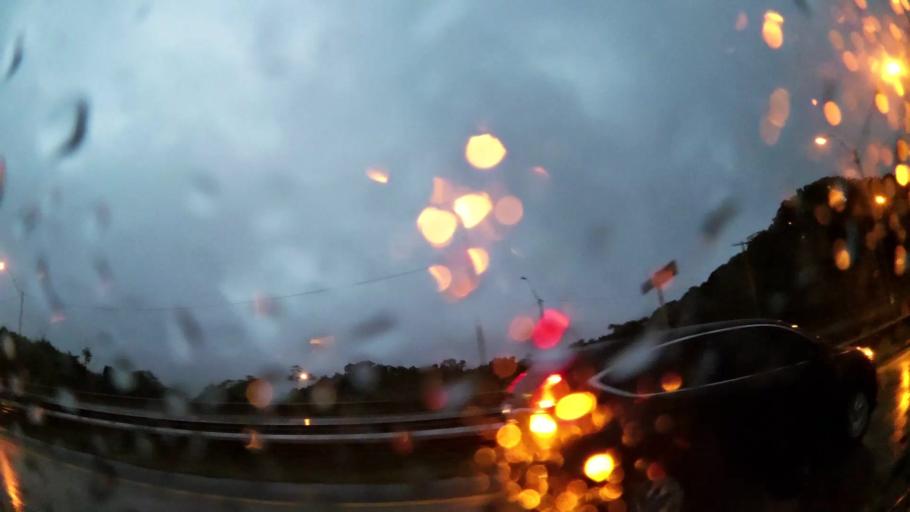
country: PA
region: Panama
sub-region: Distrito de Panama
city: Paraiso
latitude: 9.0218
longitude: -79.6396
